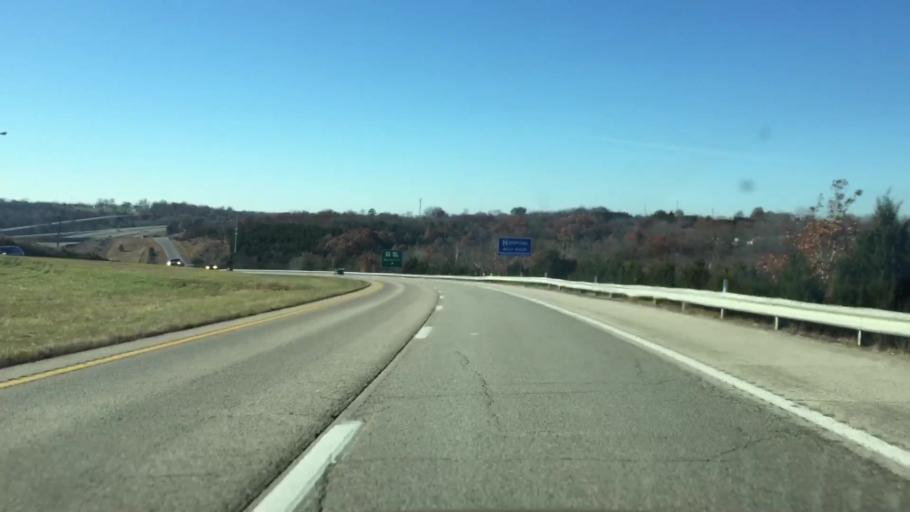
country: US
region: Missouri
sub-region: Cole County
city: Jefferson City
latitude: 38.5473
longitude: -92.2063
